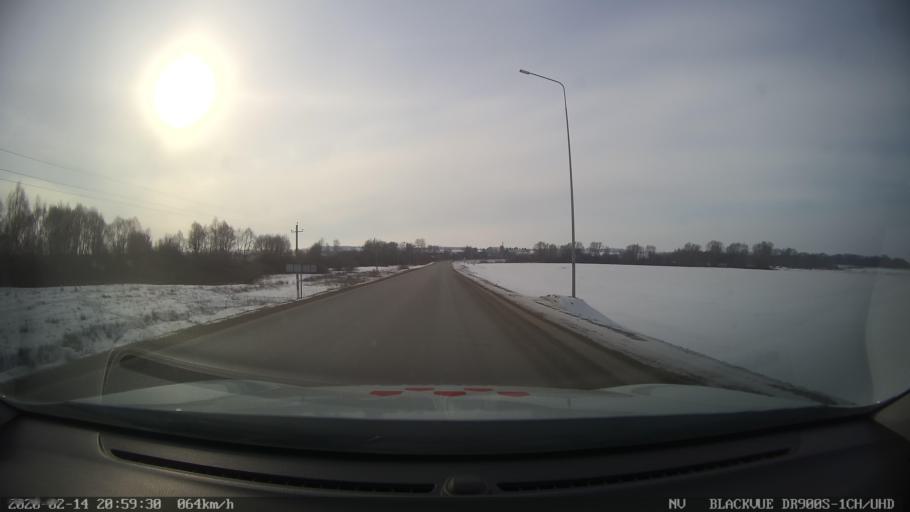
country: RU
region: Tatarstan
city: Kuybyshevskiy Zaton
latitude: 55.1781
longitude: 49.2374
